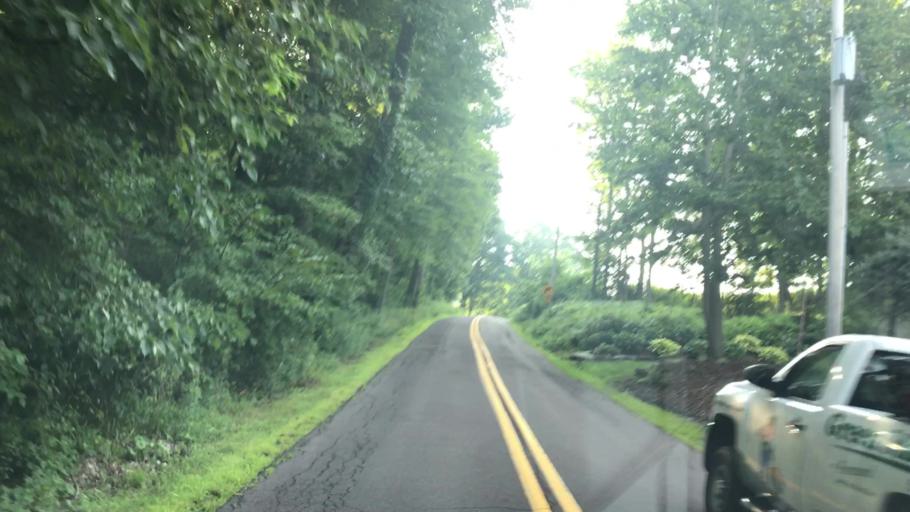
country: US
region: Pennsylvania
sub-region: Wyoming County
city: Factoryville
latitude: 41.6169
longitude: -75.7482
